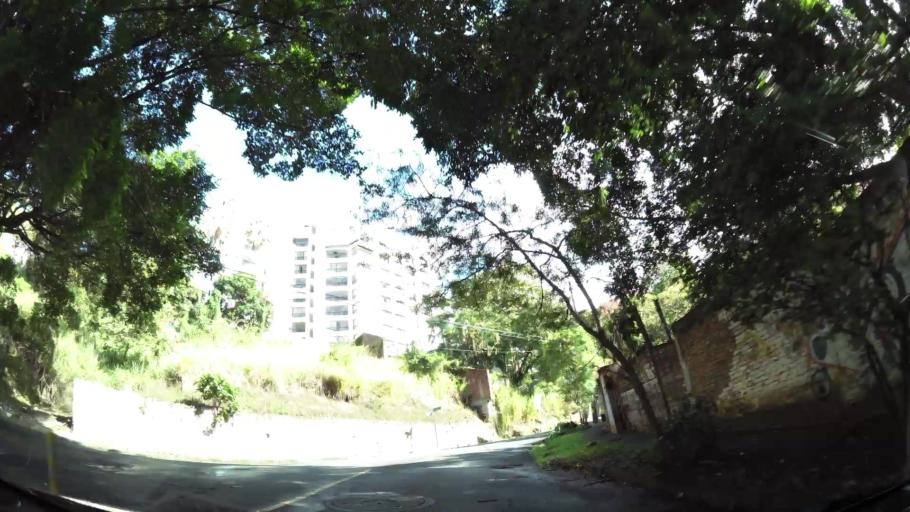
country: CO
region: Valle del Cauca
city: Cali
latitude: 3.4546
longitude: -76.5388
